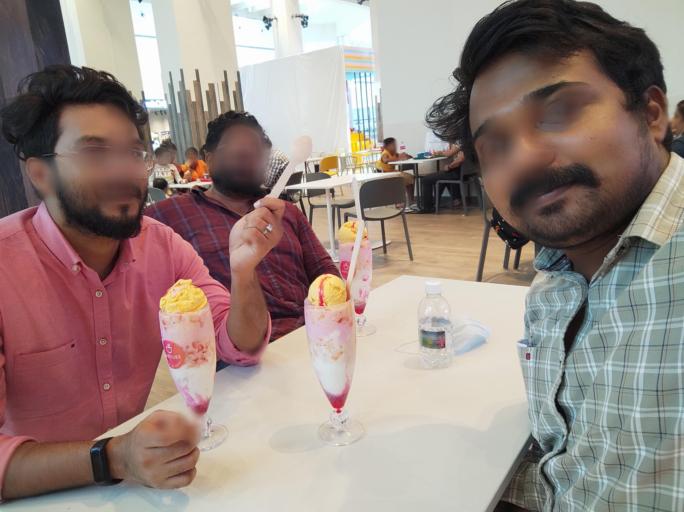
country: IN
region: Kerala
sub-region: Thiruvananthapuram
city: Thiruvananthapuram
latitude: 8.5150
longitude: 76.8983
